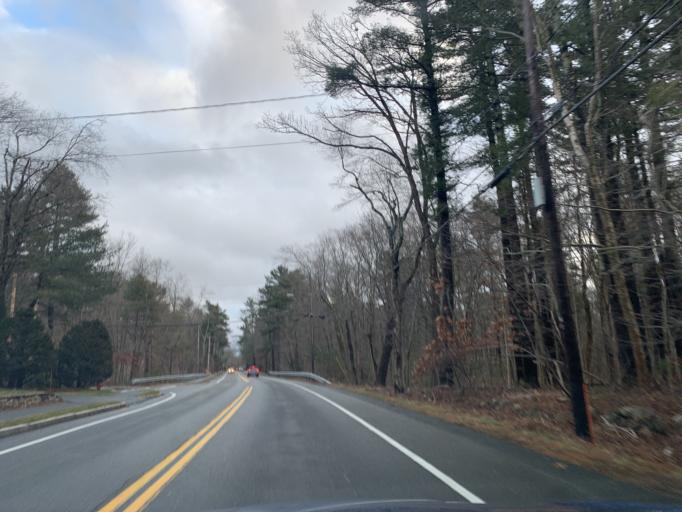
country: US
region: Massachusetts
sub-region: Norfolk County
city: Wrentham
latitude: 42.0853
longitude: -71.2913
